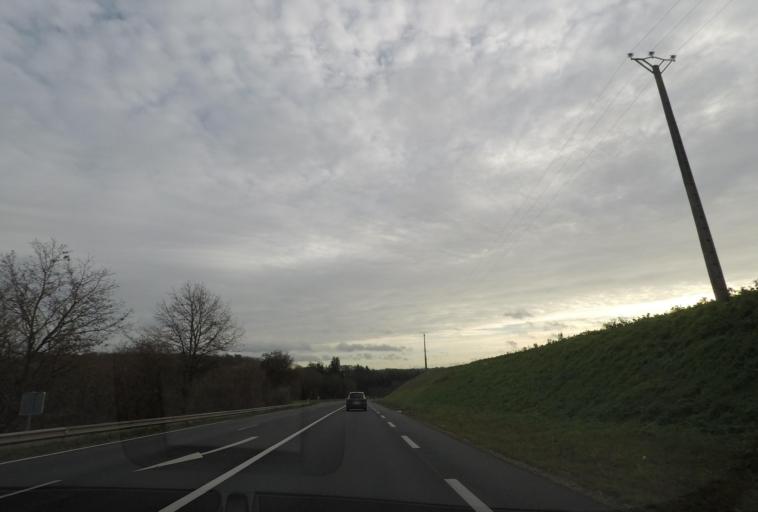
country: FR
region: Centre
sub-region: Departement du Loir-et-Cher
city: Sarge-sur-Braye
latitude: 47.9165
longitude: 0.8282
